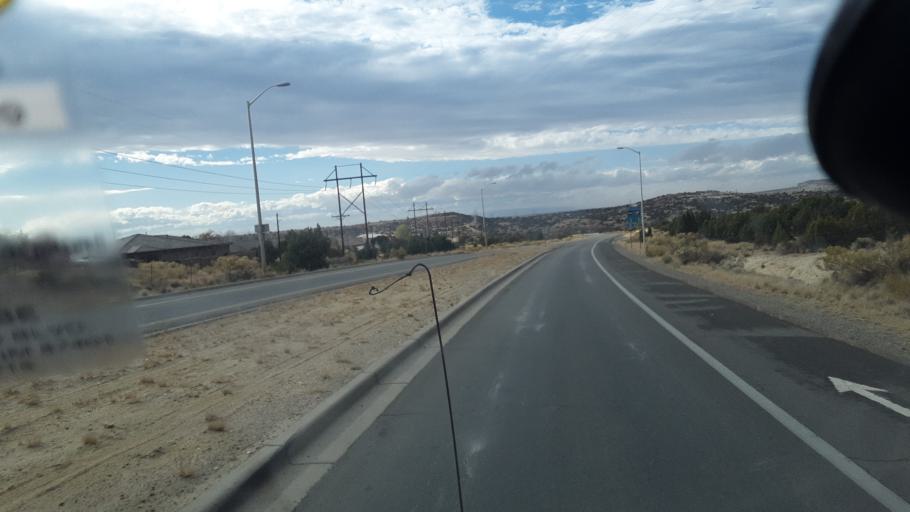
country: US
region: New Mexico
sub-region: San Juan County
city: Farmington
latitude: 36.7737
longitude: -108.1949
